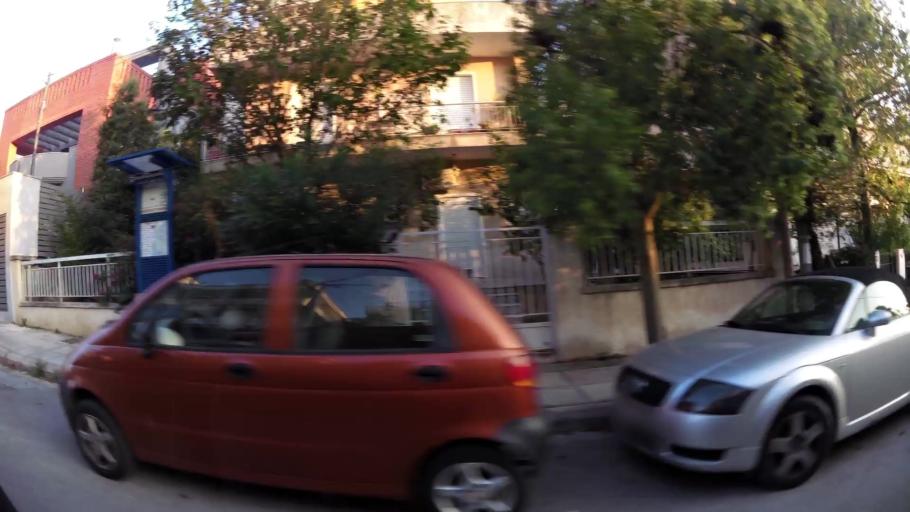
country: GR
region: Attica
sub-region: Nomarchia Athinas
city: Glyfada
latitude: 37.8820
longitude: 23.7655
